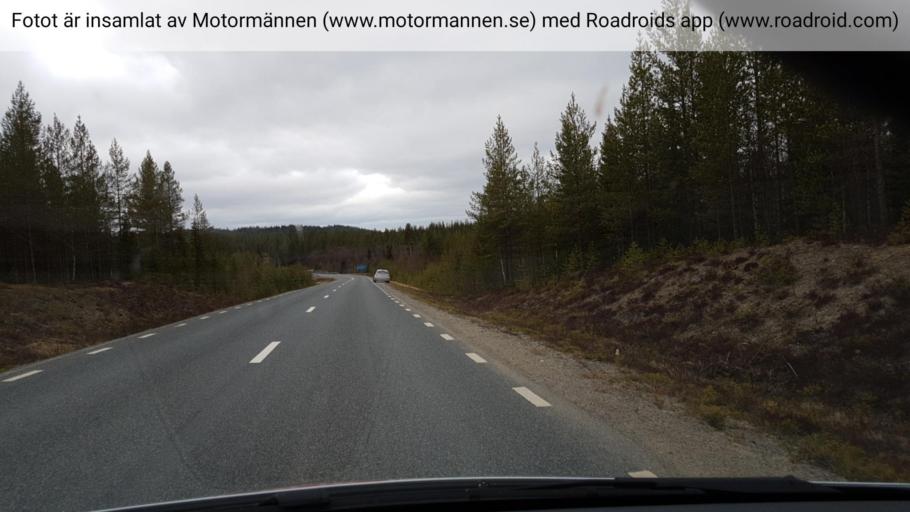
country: SE
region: Vaesternorrland
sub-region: OErnskoeldsviks Kommun
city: Bredbyn
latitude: 63.8626
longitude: 18.4811
